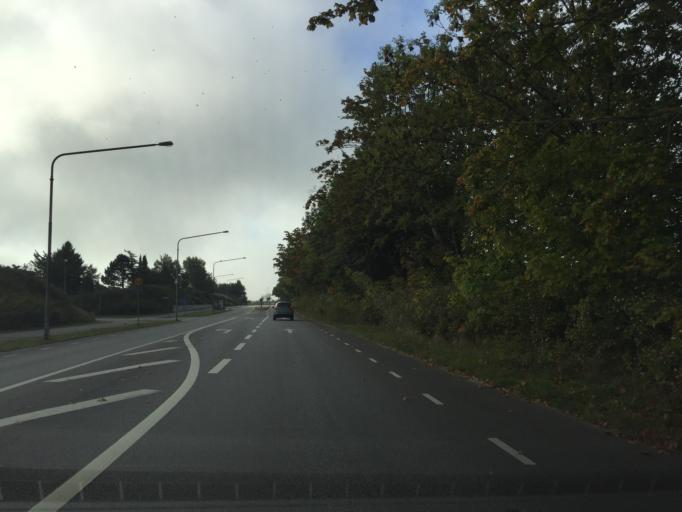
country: SE
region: Skane
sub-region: Staffanstorps Kommun
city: Staffanstorp
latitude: 55.6349
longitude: 13.1863
